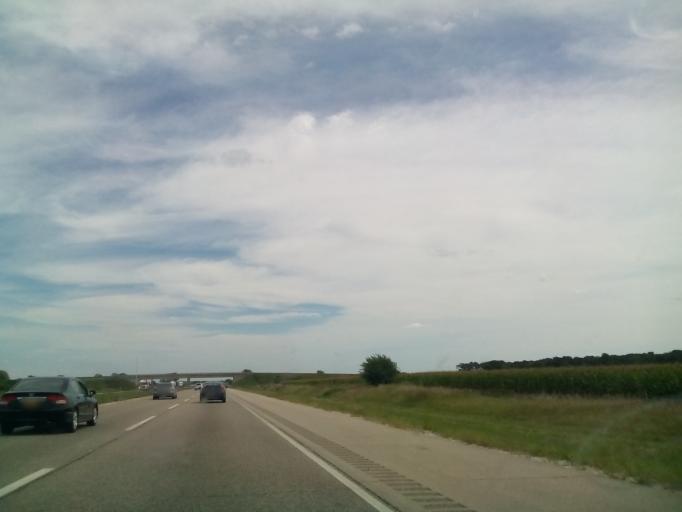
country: US
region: Illinois
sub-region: Kane County
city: Maple Park
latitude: 41.8651
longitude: -88.5656
